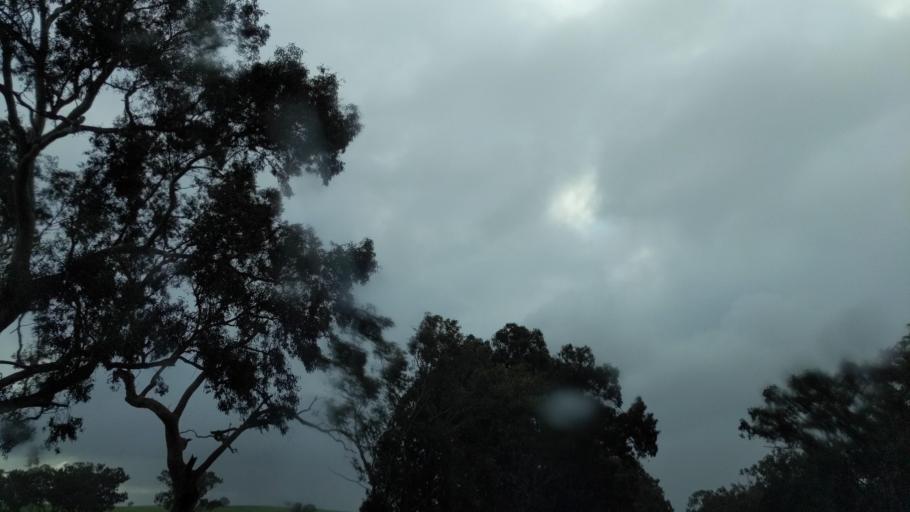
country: AU
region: New South Wales
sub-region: Wagga Wagga
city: Wagga Wagga
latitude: -34.9548
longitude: 147.3184
